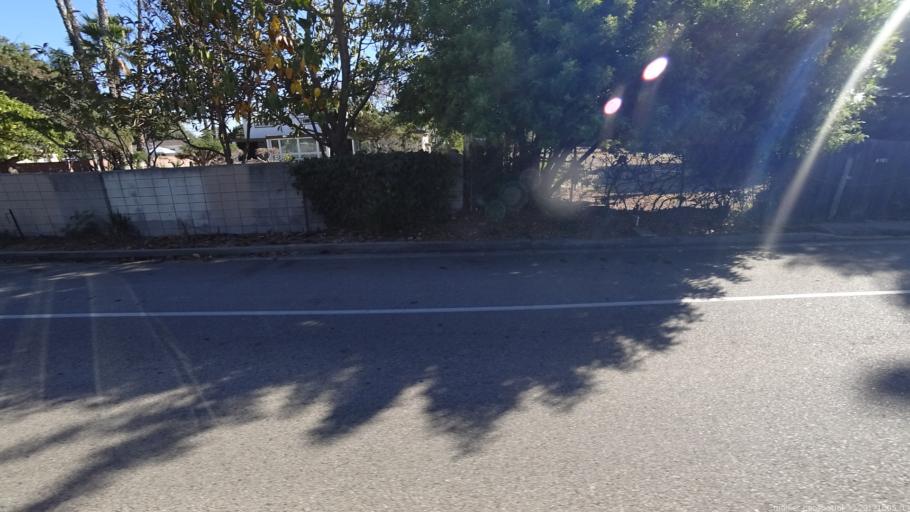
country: US
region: California
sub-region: Orange County
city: Garden Grove
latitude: 33.7776
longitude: -117.9617
